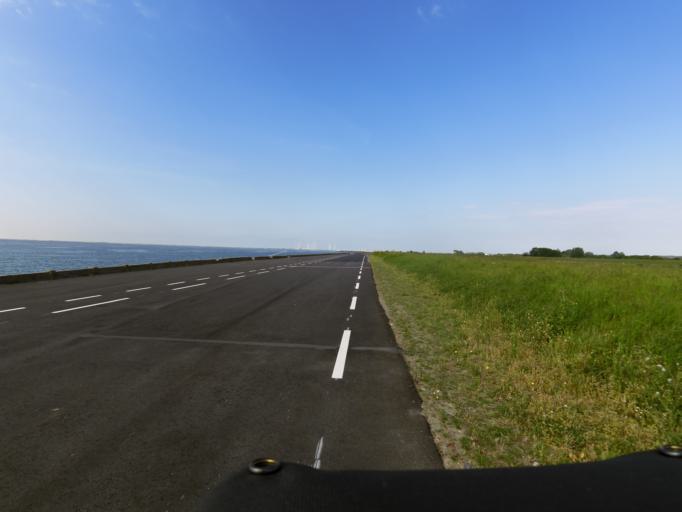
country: NL
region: Zeeland
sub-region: Schouwen-Duiveland
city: Haamstede
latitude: 51.6823
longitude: 3.7730
